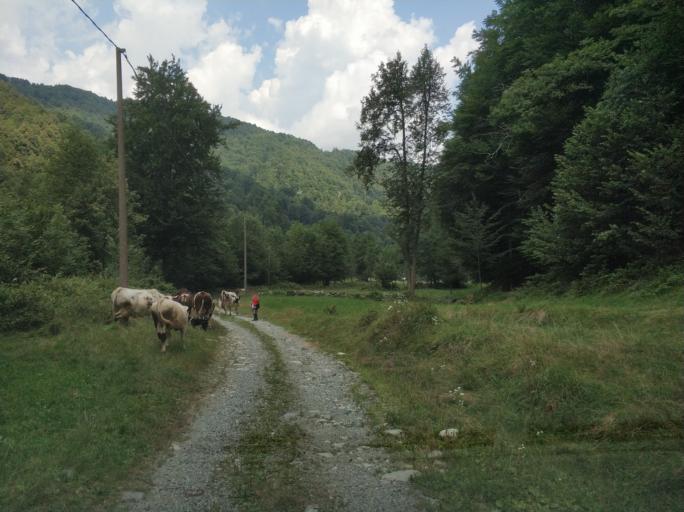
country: IT
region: Piedmont
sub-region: Provincia di Torino
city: Viu
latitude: 45.2115
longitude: 7.3939
